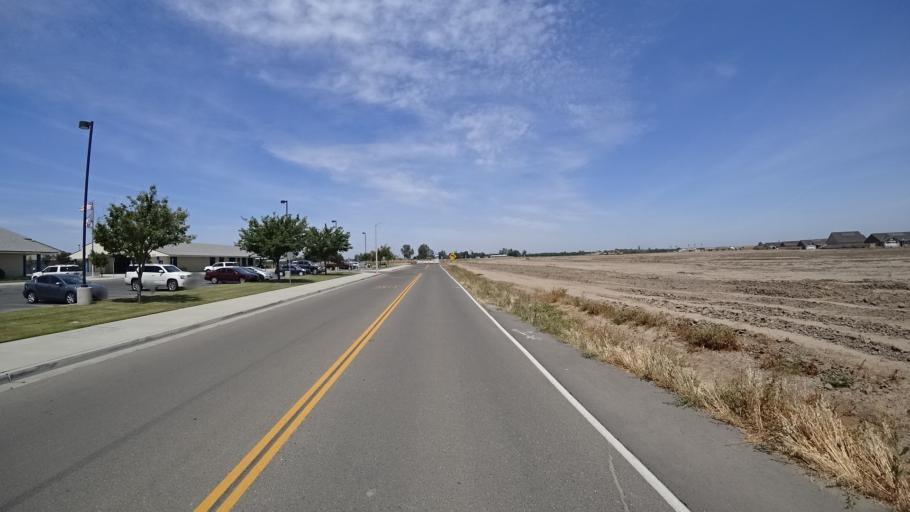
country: US
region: California
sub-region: Kings County
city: Armona
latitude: 36.3454
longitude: -119.6866
